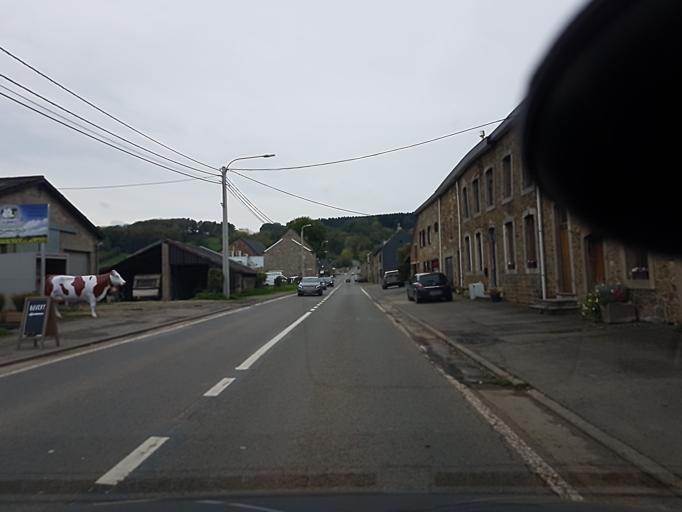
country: BE
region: Wallonia
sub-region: Province de Liege
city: Theux
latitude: 50.5341
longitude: 5.7941
